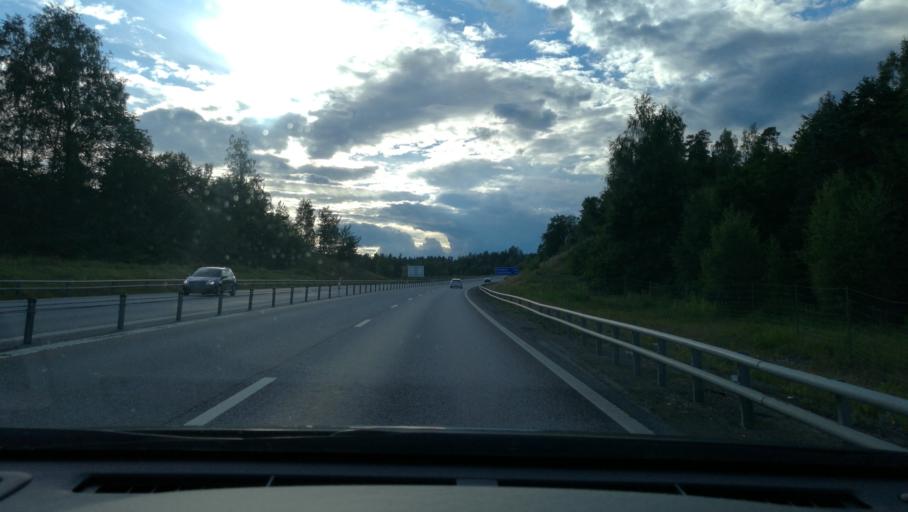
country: SE
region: OEstergoetland
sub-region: Norrkopings Kommun
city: Svartinge
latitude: 58.6476
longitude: 16.0561
